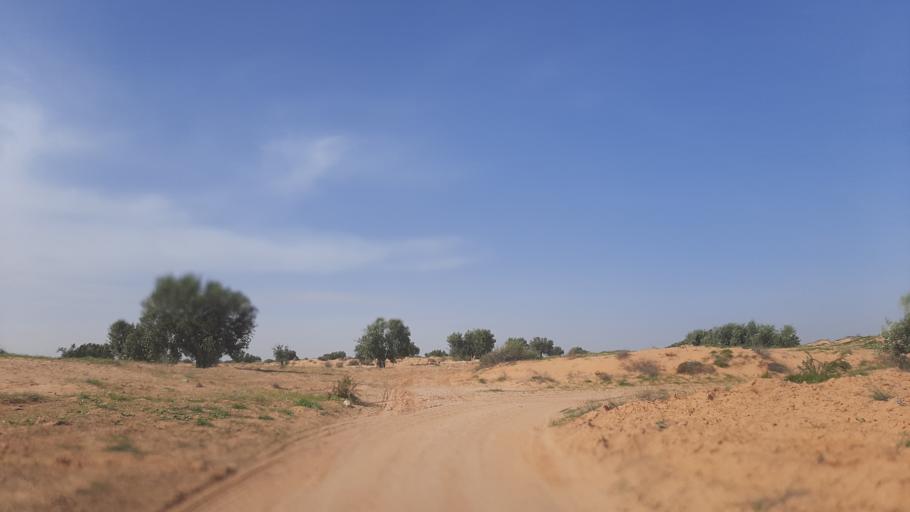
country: TN
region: Madanin
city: Zarzis
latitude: 33.4330
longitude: 10.8086
